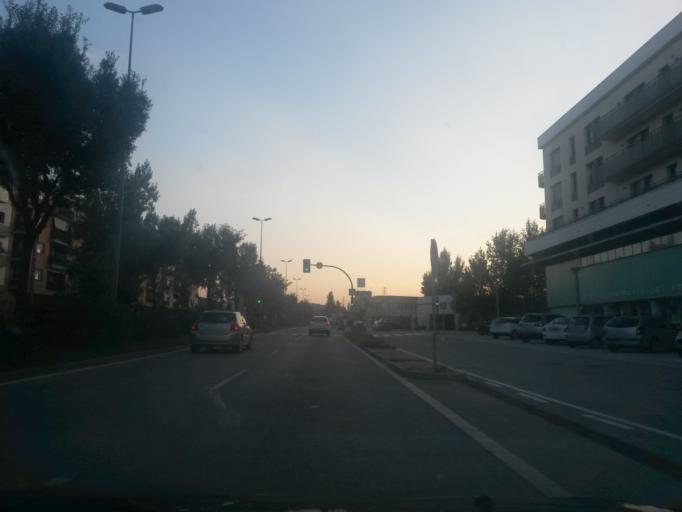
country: ES
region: Catalonia
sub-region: Provincia de Girona
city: Sarria de Ter
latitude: 42.0194
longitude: 2.8225
